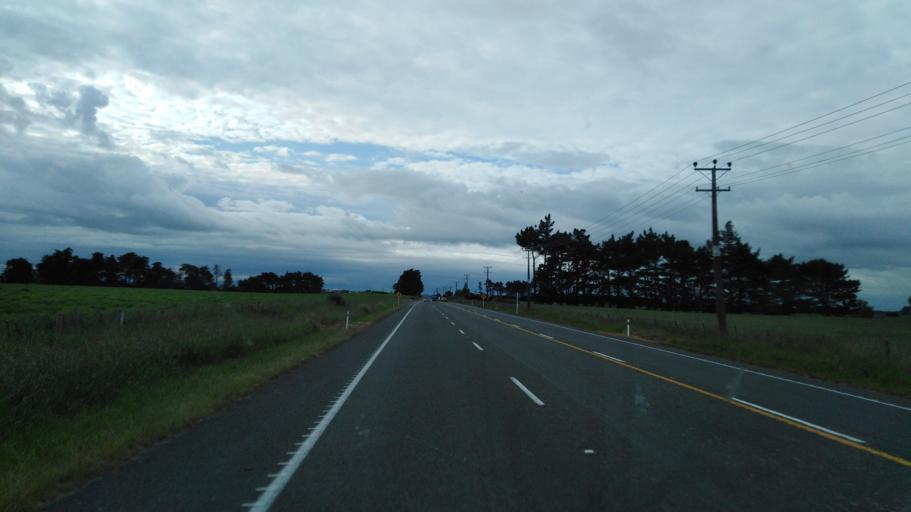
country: NZ
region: Manawatu-Wanganui
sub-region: Rangitikei District
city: Bulls
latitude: -40.1348
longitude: 175.3634
